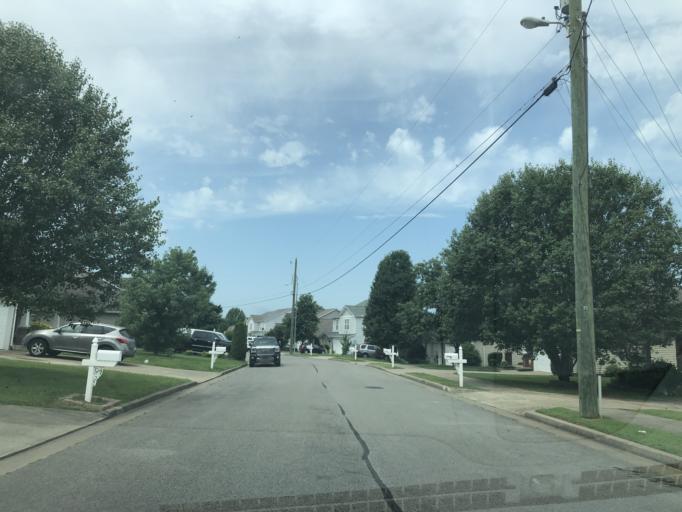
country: US
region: Tennessee
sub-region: Williamson County
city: Nolensville
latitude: 36.0224
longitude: -86.6719
